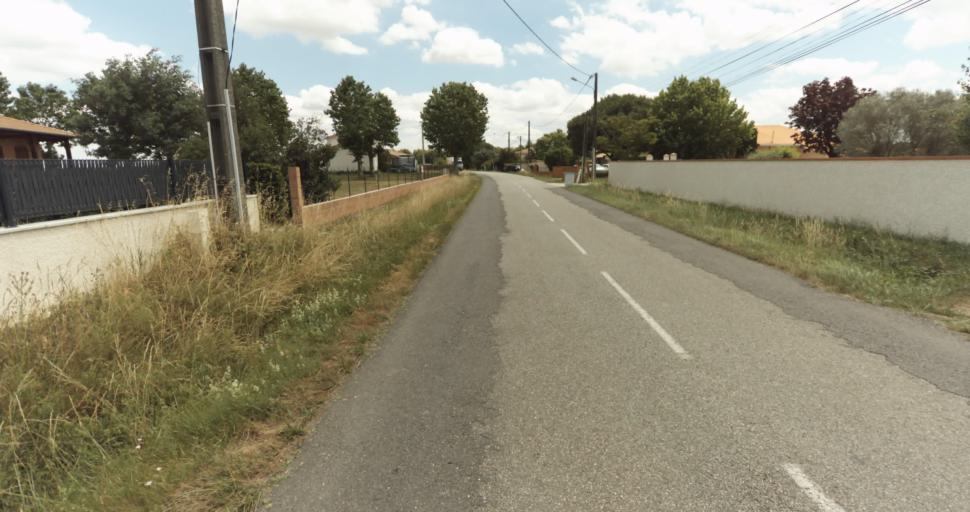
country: FR
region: Midi-Pyrenees
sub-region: Departement de la Haute-Garonne
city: Fontenilles
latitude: 43.5465
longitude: 1.1823
